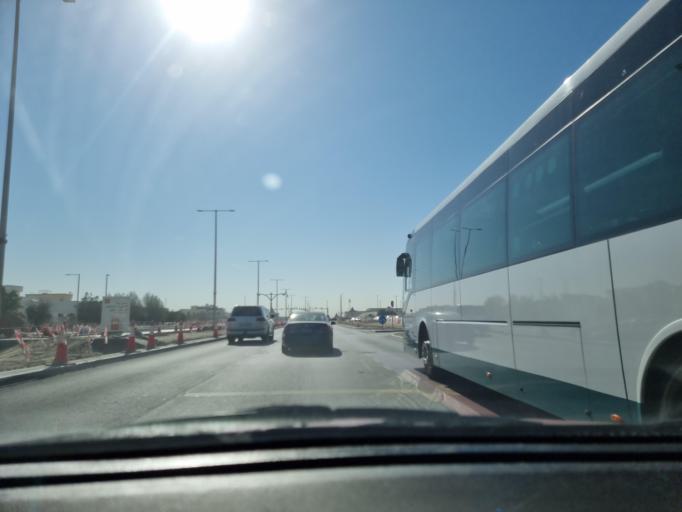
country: AE
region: Abu Dhabi
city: Abu Dhabi
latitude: 24.4215
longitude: 54.5660
